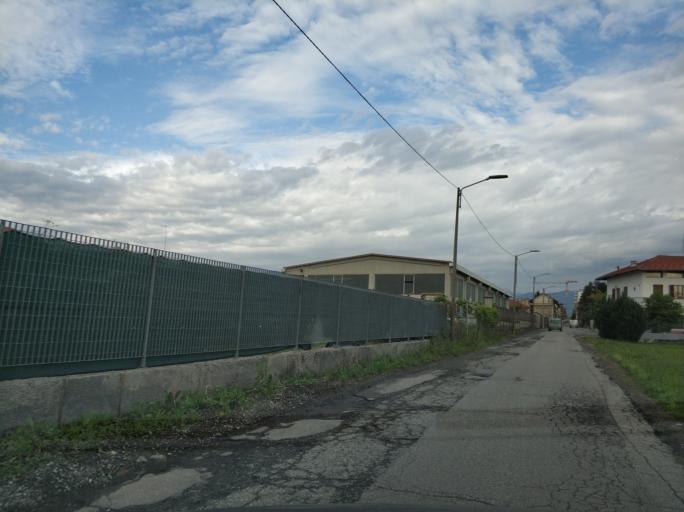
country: IT
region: Piedmont
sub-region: Provincia di Torino
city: Cirie
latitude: 45.2268
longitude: 7.6104
